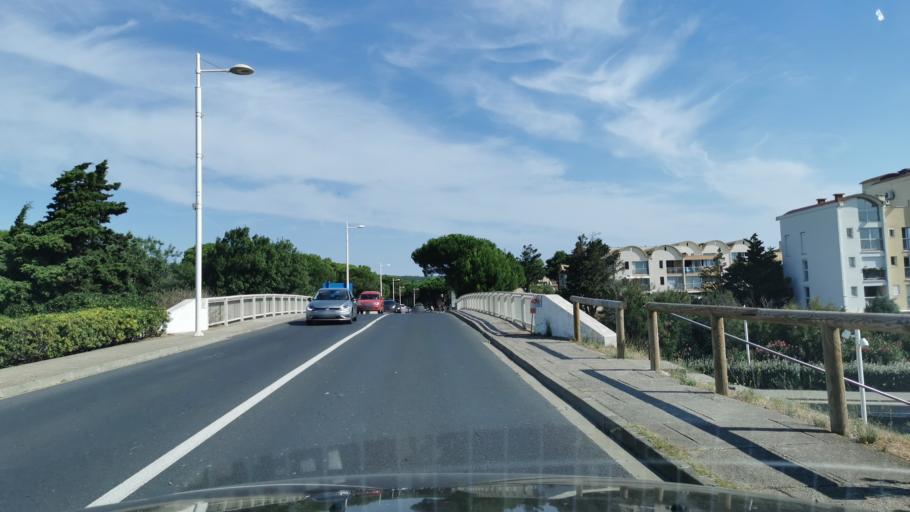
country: FR
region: Languedoc-Roussillon
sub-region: Departement de l'Aude
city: Gruissan
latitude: 43.1095
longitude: 3.0920
